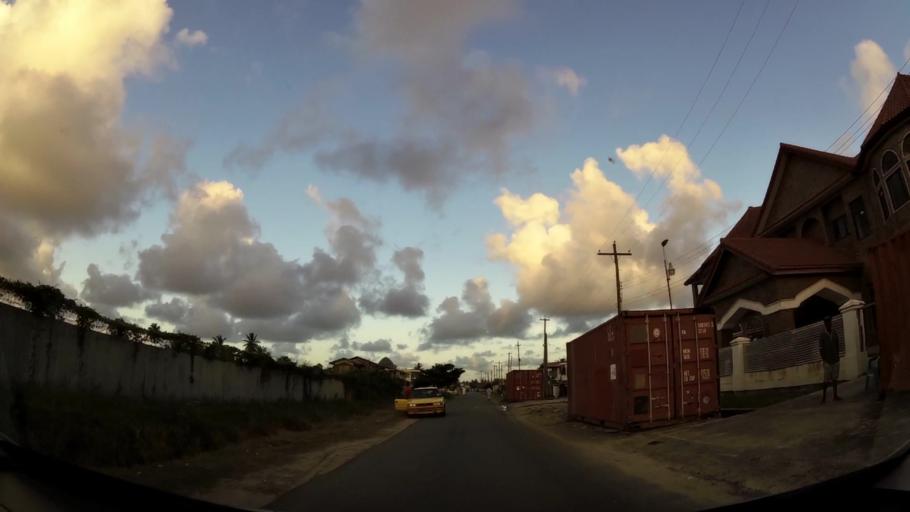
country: GY
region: Demerara-Mahaica
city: Georgetown
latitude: 6.8147
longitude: -58.1033
